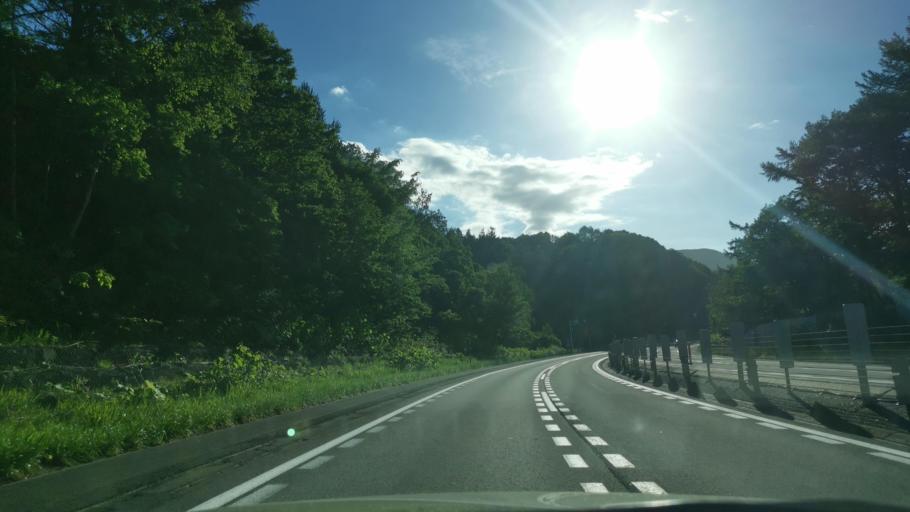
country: JP
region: Hokkaido
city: Otaru
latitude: 43.1509
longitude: 141.1195
